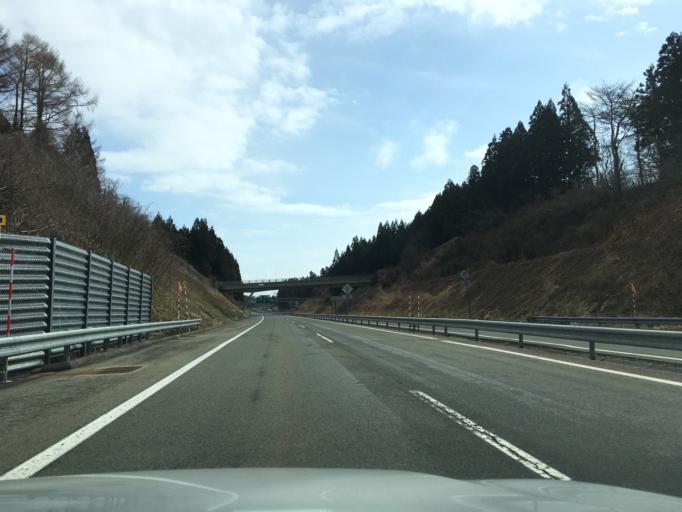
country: JP
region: Akita
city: Akita
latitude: 39.6376
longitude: 140.1991
